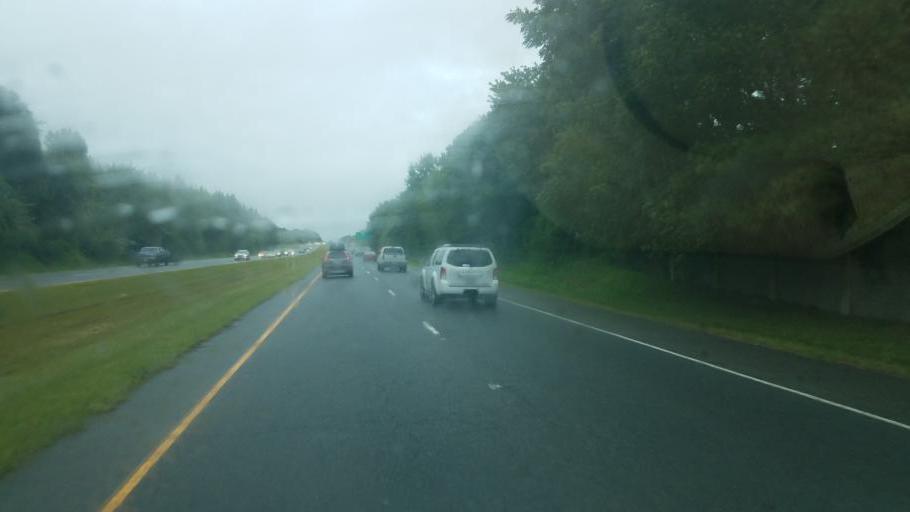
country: US
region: Virginia
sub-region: City of Chesapeake
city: Chesapeake
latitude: 36.7023
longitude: -76.2265
